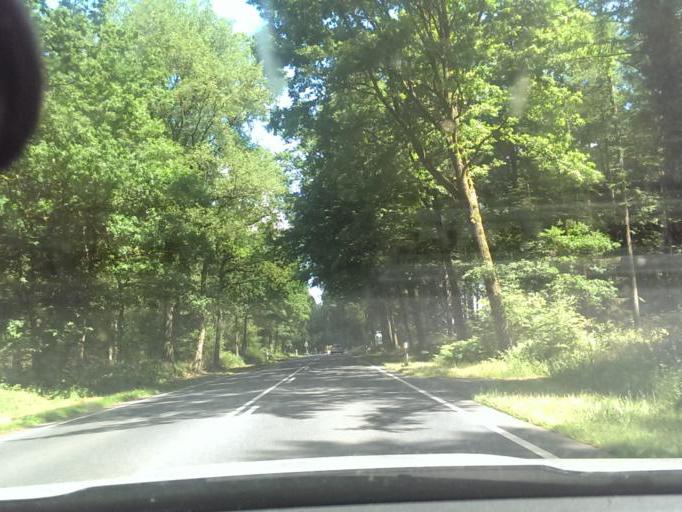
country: DE
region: Lower Saxony
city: Kirchlinteln
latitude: 52.9996
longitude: 9.2690
